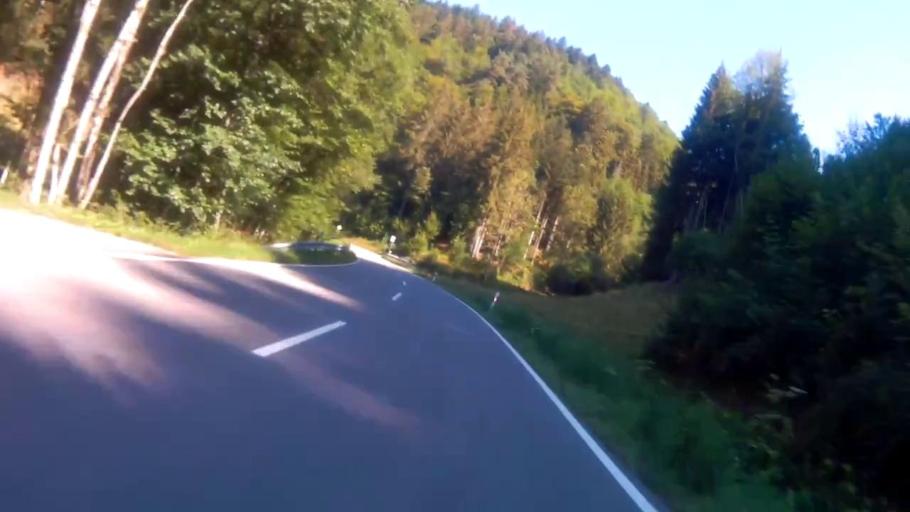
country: DE
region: Baden-Wuerttemberg
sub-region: Freiburg Region
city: Zell im Wiesental
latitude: 47.7355
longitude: 7.7698
